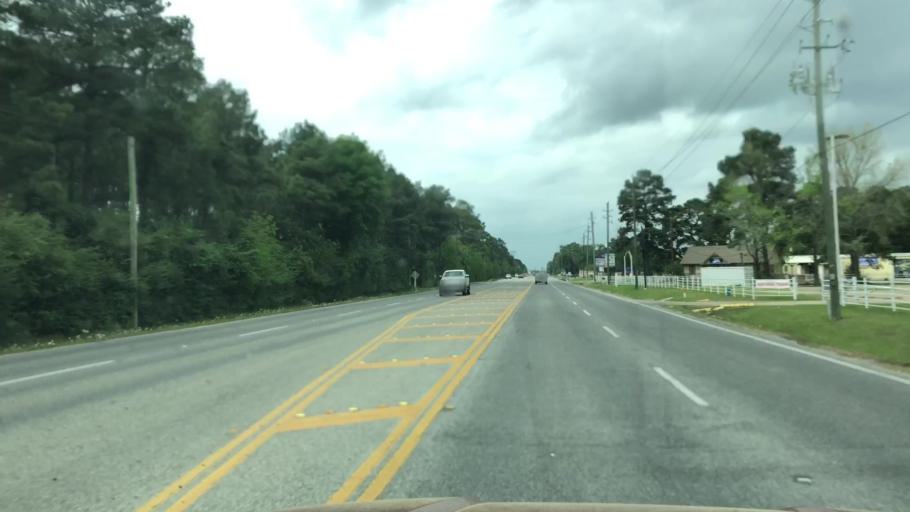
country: US
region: Texas
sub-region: Harris County
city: Spring
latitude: 30.0608
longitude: -95.4979
